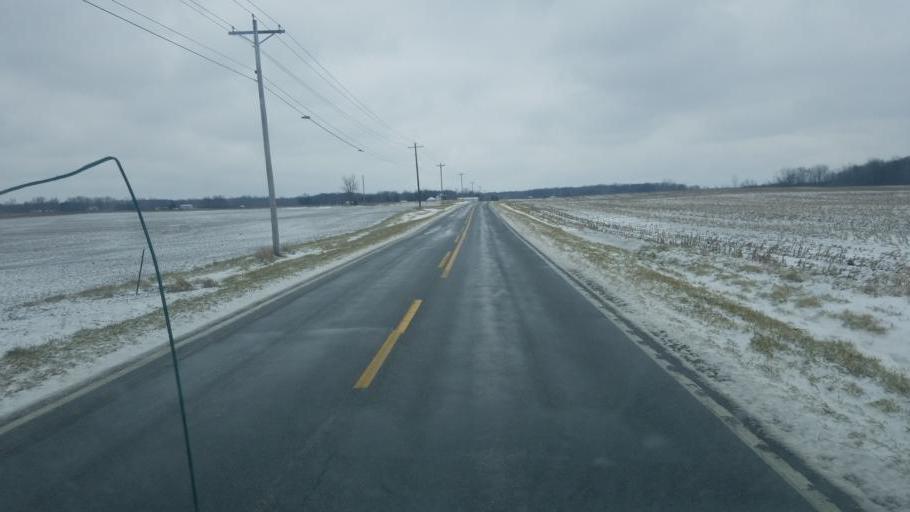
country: US
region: Ohio
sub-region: Delaware County
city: Sunbury
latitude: 40.3184
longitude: -82.8069
